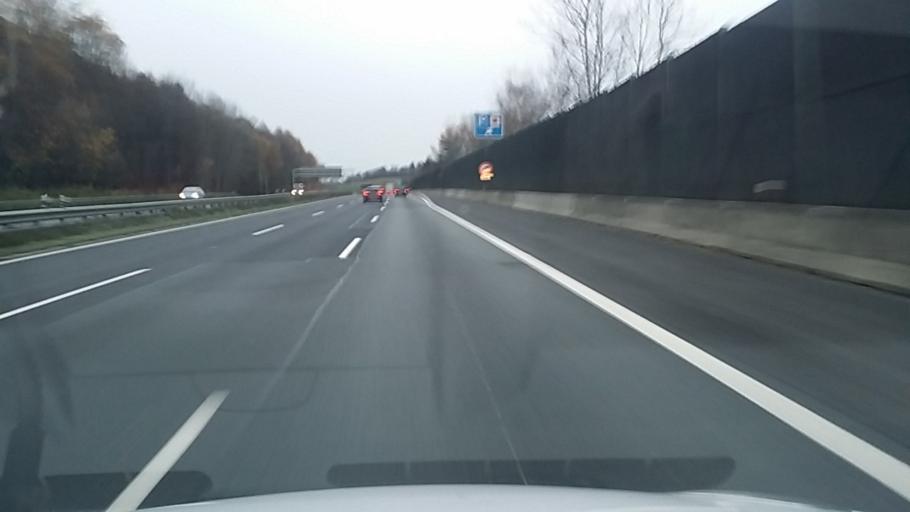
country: CZ
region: Central Bohemia
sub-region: Okres Praha-Vychod
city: Mnichovice
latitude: 49.9284
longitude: 14.6978
